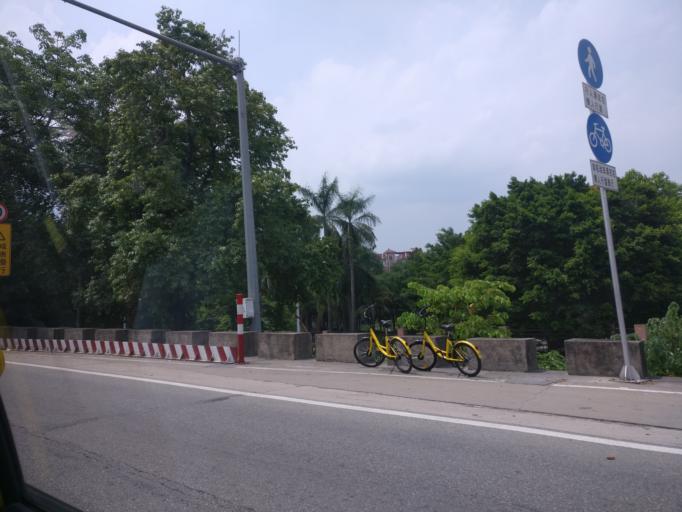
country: CN
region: Guangdong
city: Luopu
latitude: 23.0457
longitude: 113.2974
